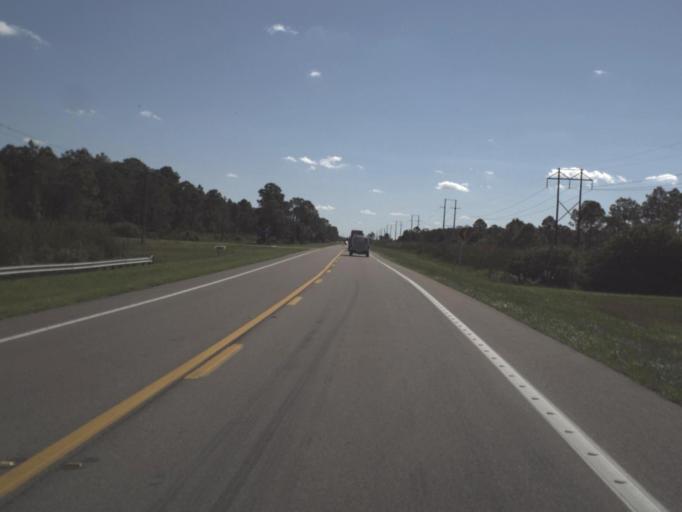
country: US
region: Florida
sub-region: Lee County
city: Lehigh Acres
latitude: 26.5350
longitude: -81.6287
